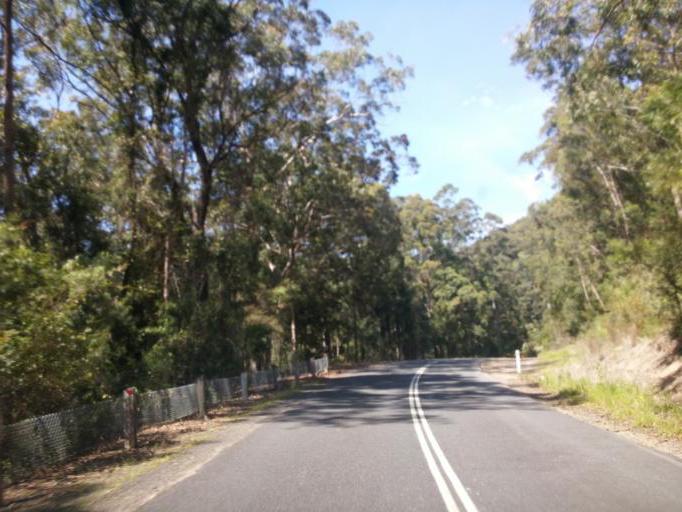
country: AU
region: New South Wales
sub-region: Great Lakes
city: Bulahdelah
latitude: -32.4044
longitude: 152.2975
